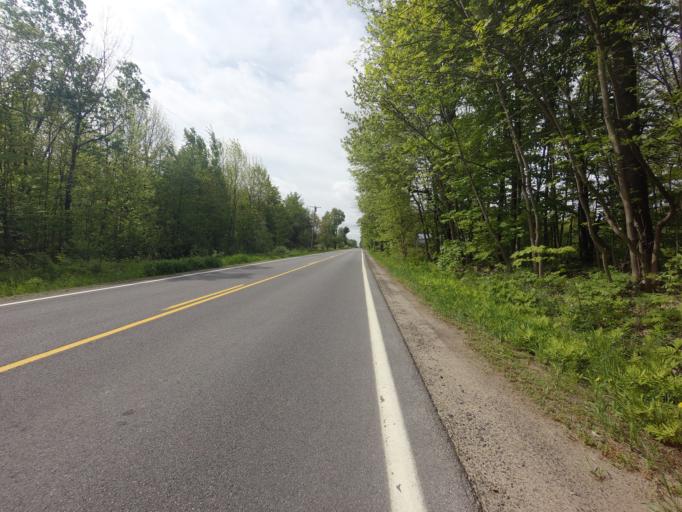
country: CA
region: Ontario
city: Cornwall
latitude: 44.7334
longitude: -74.6648
